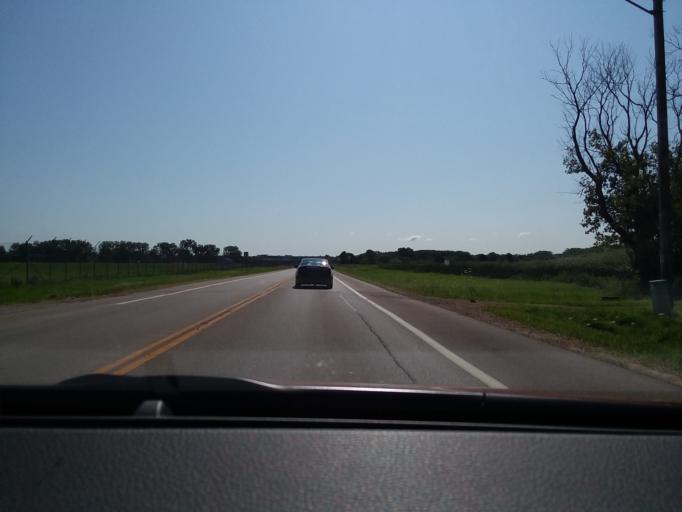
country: US
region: Wisconsin
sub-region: Dane County
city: Maple Bluff
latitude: 43.1211
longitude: -89.3460
